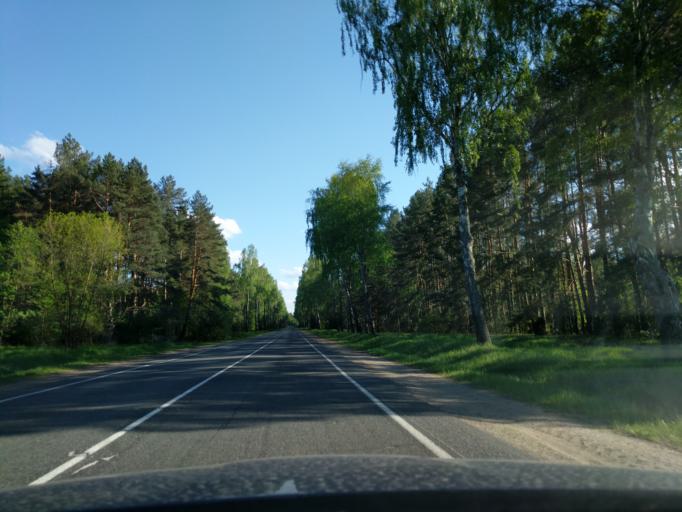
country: BY
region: Minsk
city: Myadzyel
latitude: 54.8529
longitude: 26.9250
